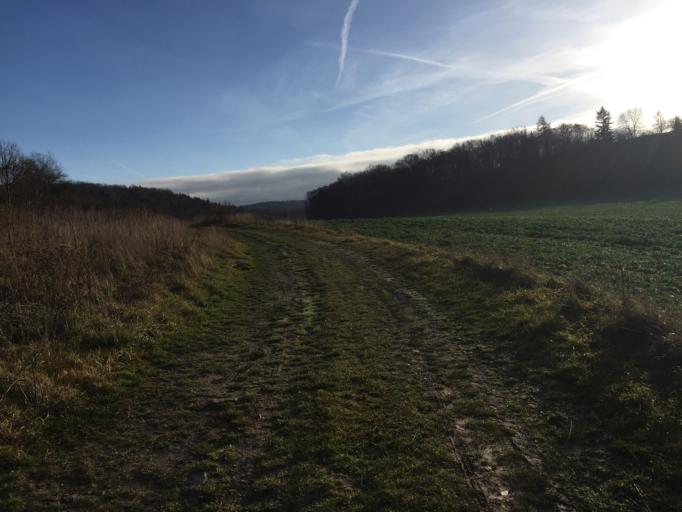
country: DE
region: Thuringia
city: Ranis
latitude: 50.6766
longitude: 11.5788
